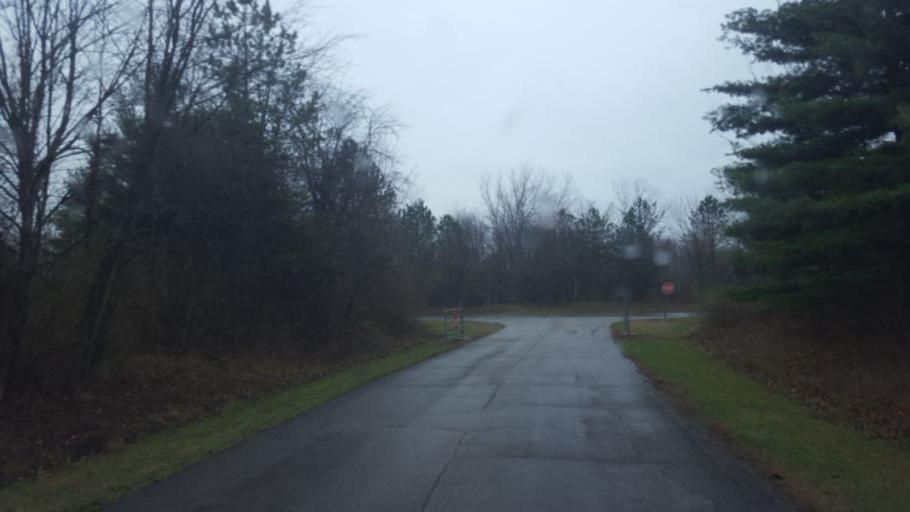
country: US
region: Ohio
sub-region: Delaware County
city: Lewis Center
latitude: 40.2127
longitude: -82.9767
